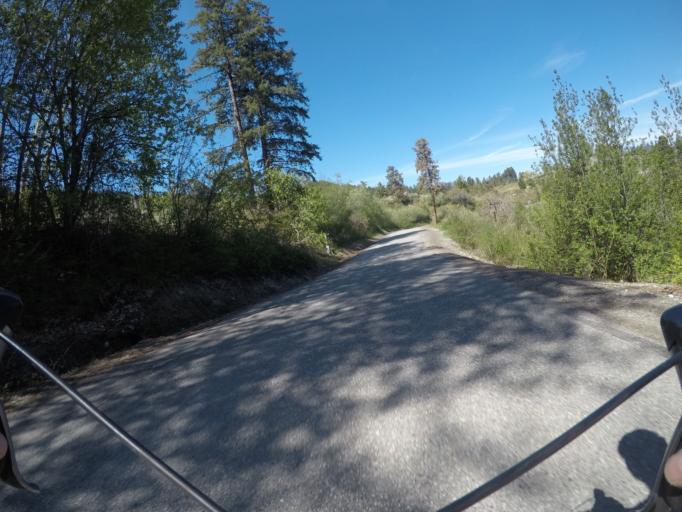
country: US
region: Washington
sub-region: Chelan County
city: Leavenworth
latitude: 47.5431
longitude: -120.5788
